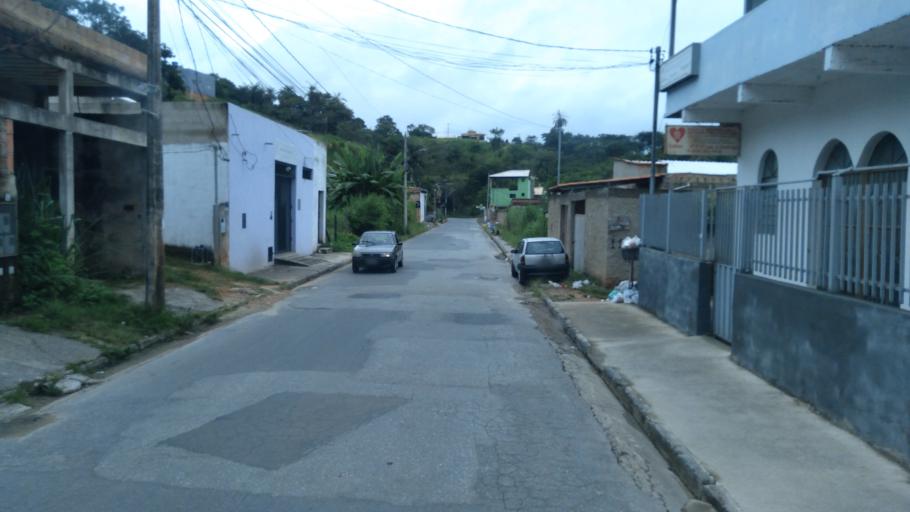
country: BR
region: Minas Gerais
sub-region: Santa Luzia
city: Santa Luzia
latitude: -19.8379
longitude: -43.8705
